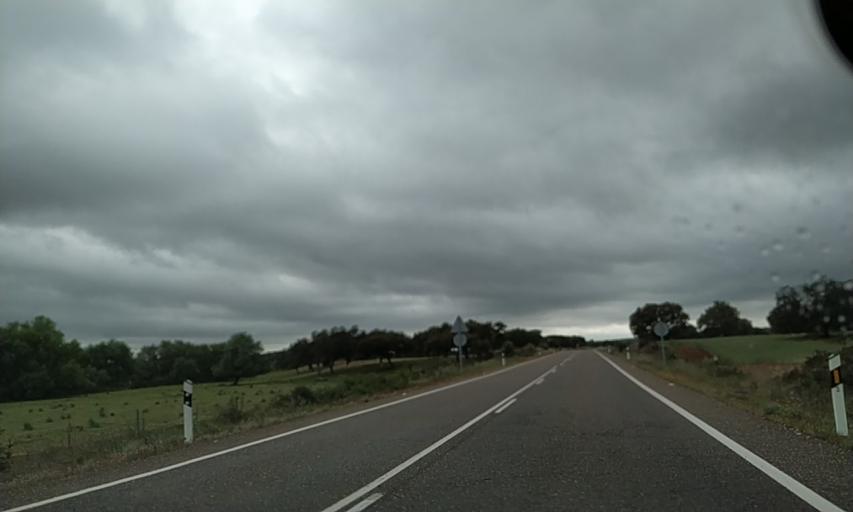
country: ES
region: Extremadura
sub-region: Provincia de Badajoz
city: La Roca de la Sierra
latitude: 39.0679
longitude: -6.7598
